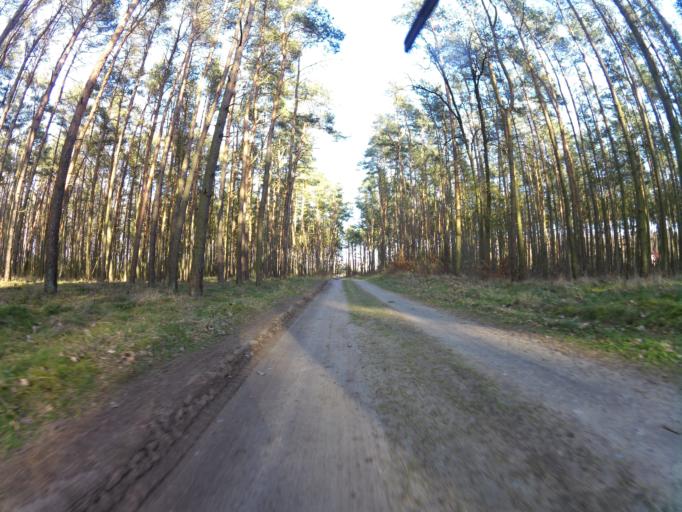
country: PL
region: West Pomeranian Voivodeship
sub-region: Powiat policki
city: Nowe Warpno
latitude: 53.7330
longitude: 14.3253
